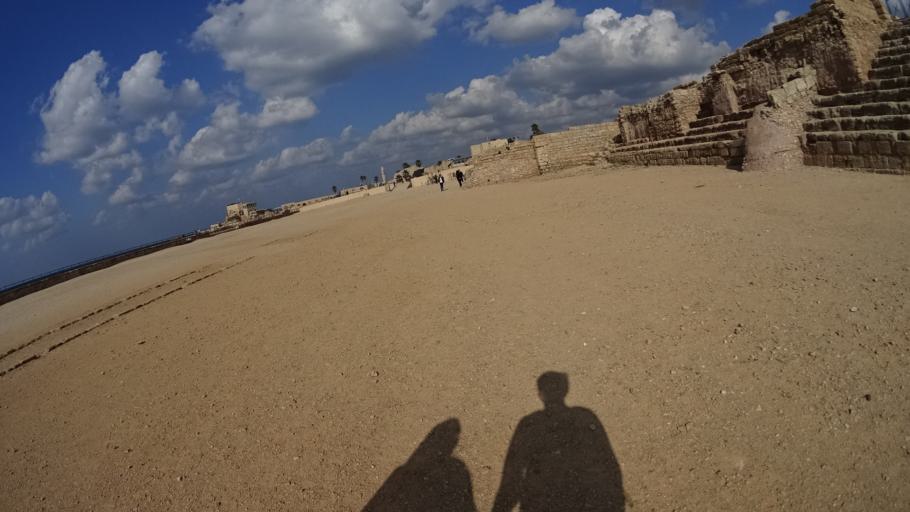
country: IL
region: Haifa
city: Qesarya
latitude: 32.4990
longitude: 34.8909
